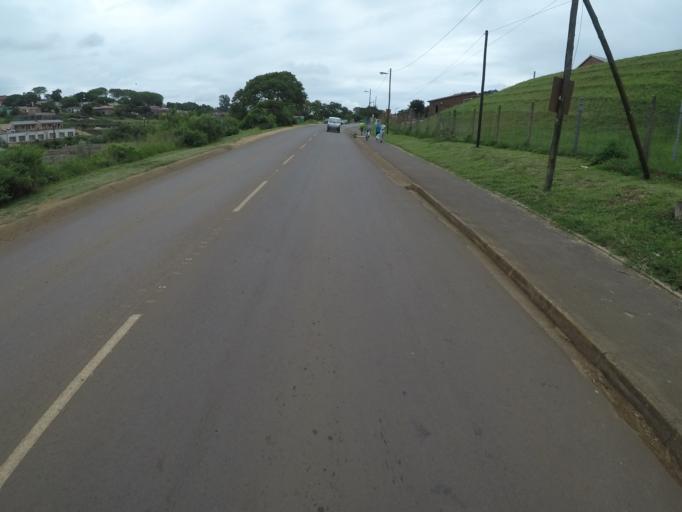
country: ZA
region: KwaZulu-Natal
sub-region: uThungulu District Municipality
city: Empangeni
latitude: -28.7794
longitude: 31.8637
